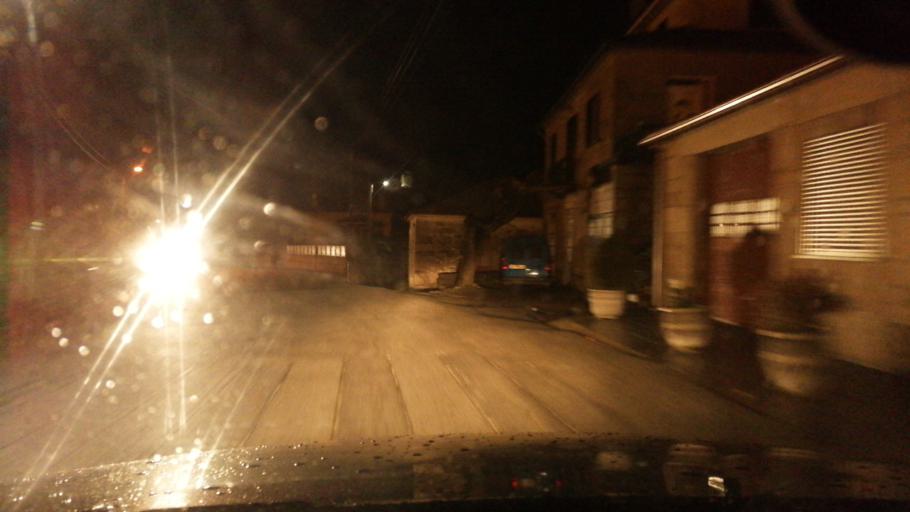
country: PT
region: Viseu
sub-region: Moimenta da Beira
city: Moimenta da Beira
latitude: 41.0404
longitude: -7.6397
